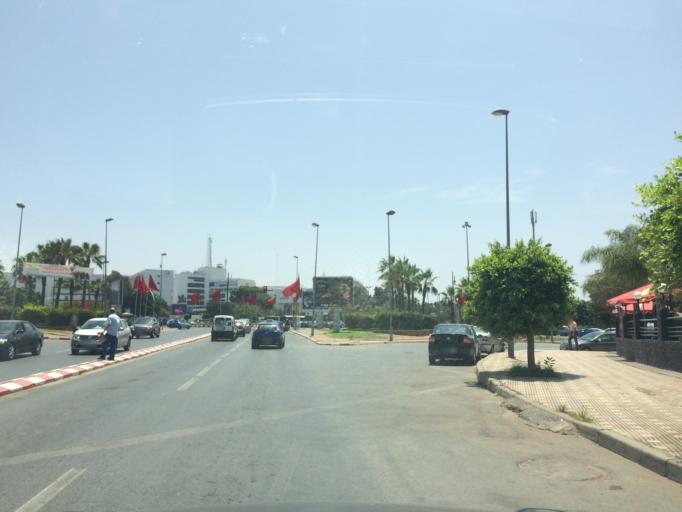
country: MA
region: Rabat-Sale-Zemmour-Zaer
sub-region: Rabat
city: Rabat
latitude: 33.9877
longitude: -6.8516
